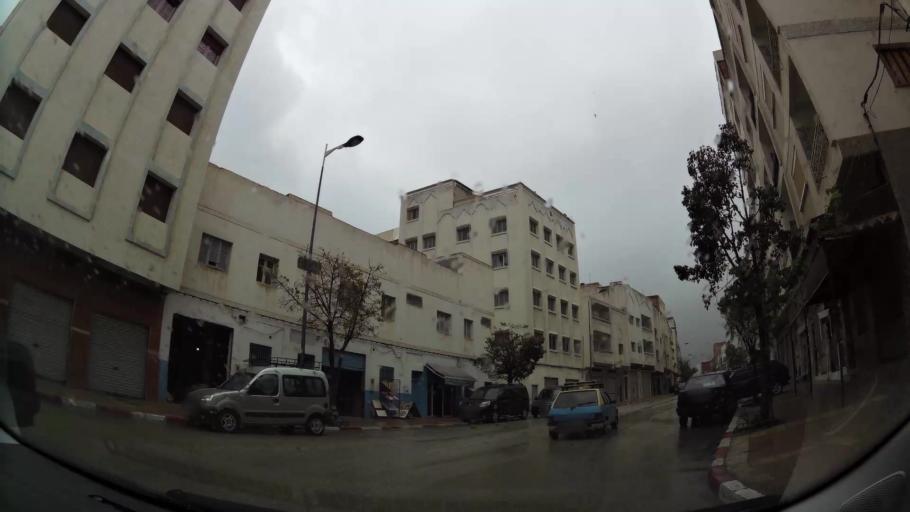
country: MA
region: Taza-Al Hoceima-Taounate
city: Al Hoceima
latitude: 35.2514
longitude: -3.9388
